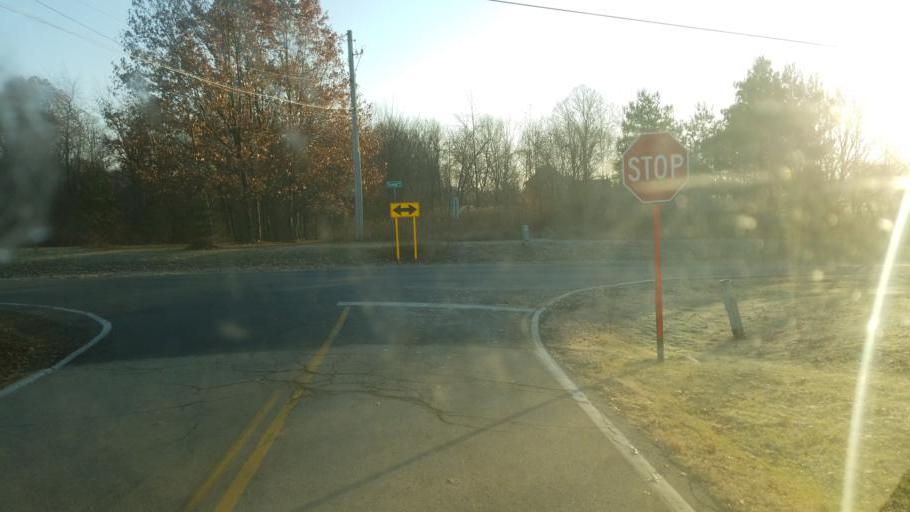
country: US
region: Ohio
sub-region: Medina County
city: Seville
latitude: 41.0624
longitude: -81.8152
